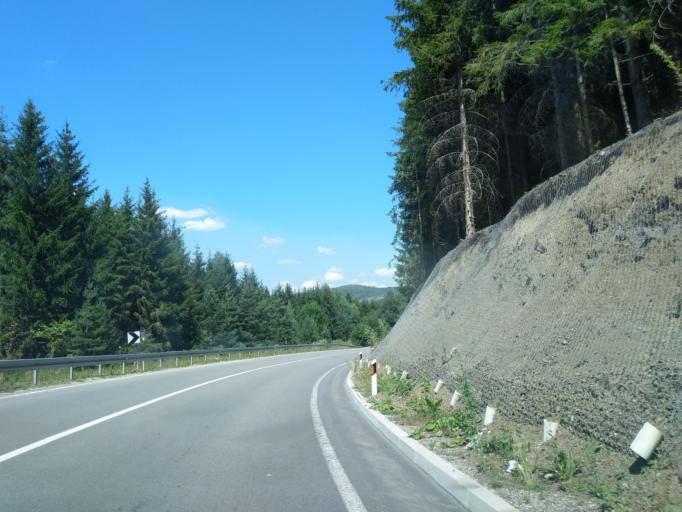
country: RS
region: Central Serbia
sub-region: Zlatiborski Okrug
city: Sjenica
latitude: 43.3168
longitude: 19.8925
